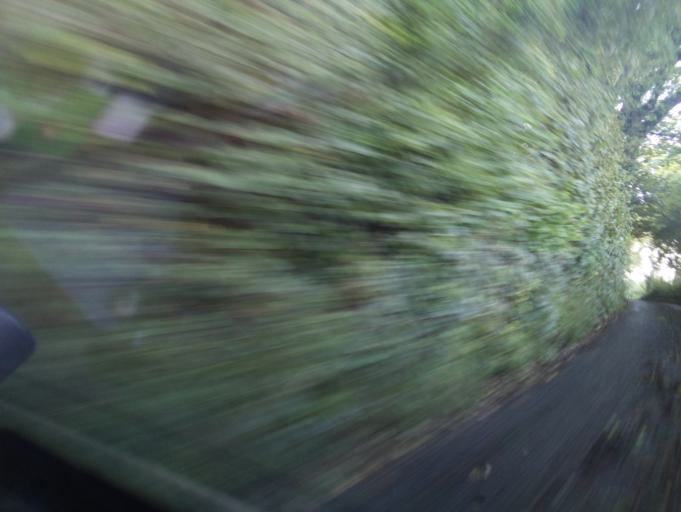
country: GB
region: England
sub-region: Devon
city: Dartmouth
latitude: 50.3382
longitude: -3.6036
